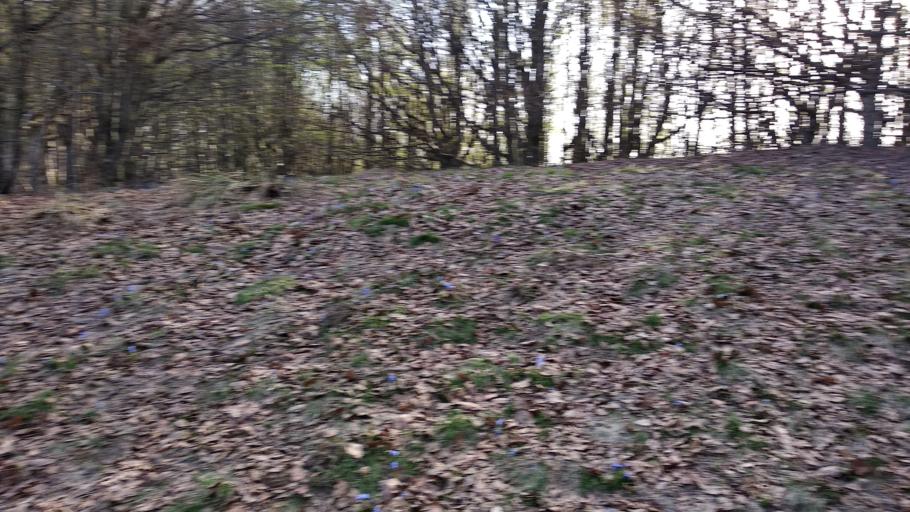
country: IT
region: Tuscany
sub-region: Province of Arezzo
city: Stia
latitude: 43.8670
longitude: 11.7282
